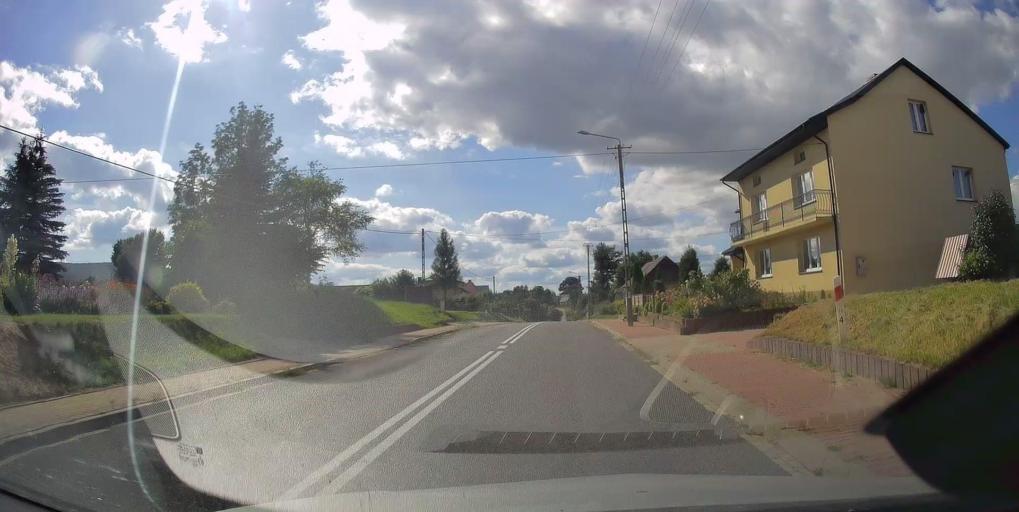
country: PL
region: Swietokrzyskie
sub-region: Powiat kielecki
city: Nowa Slupia
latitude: 50.8833
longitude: 21.0500
